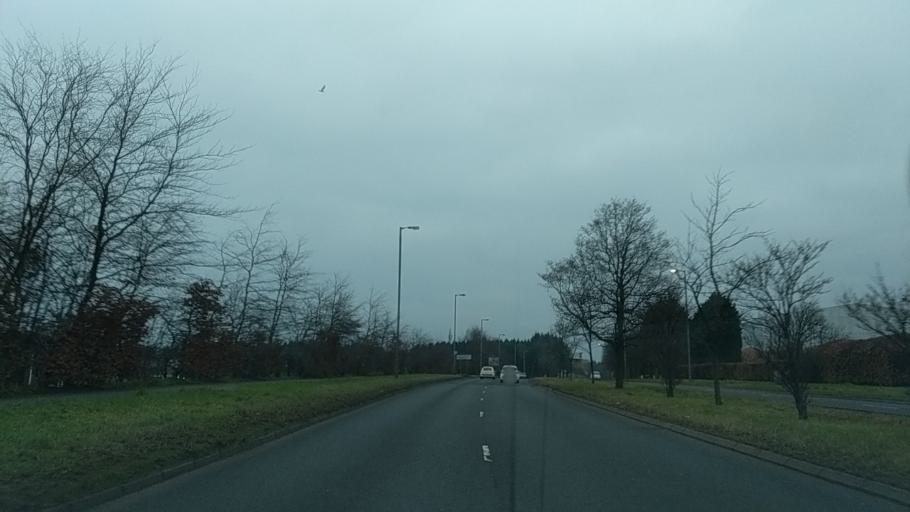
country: GB
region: Scotland
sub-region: Glasgow City
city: Carmunnock
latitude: 55.7660
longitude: -4.2145
